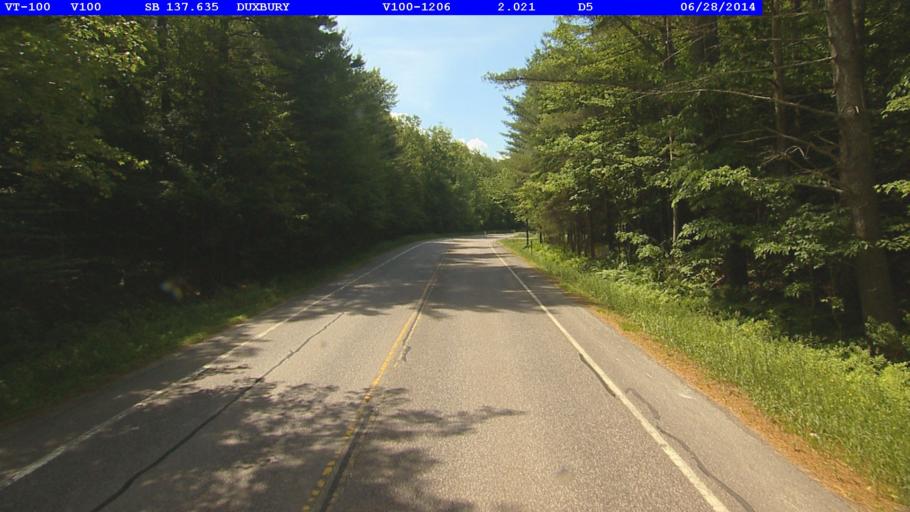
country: US
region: Vermont
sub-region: Washington County
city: Waterbury
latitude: 44.2749
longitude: -72.7846
